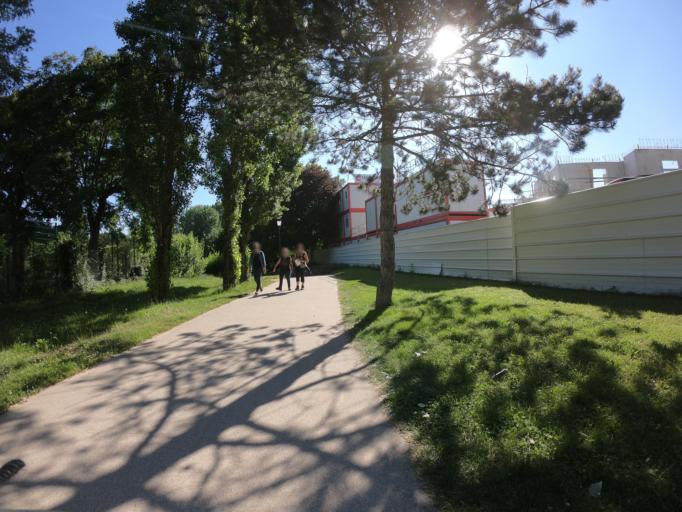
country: FR
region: Ile-de-France
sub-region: Departement des Hauts-de-Seine
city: Antony
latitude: 48.7445
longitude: 2.2877
